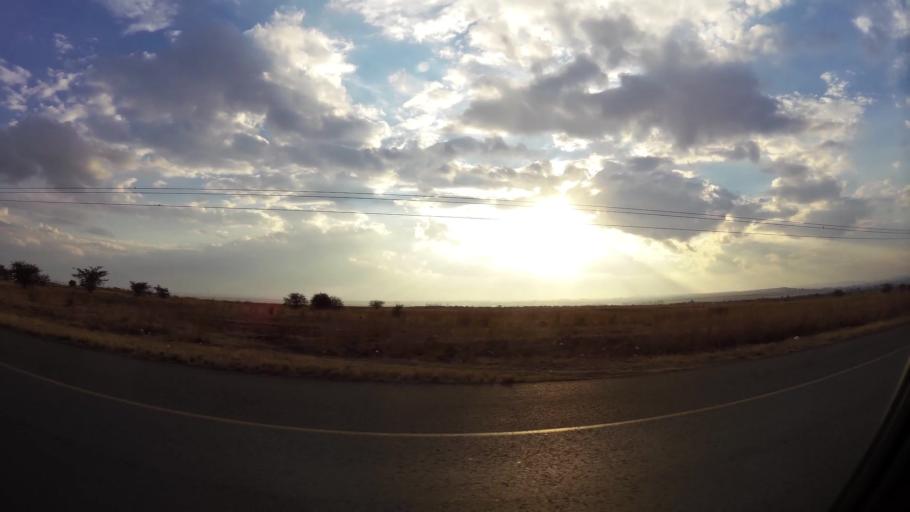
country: ZA
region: Gauteng
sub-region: Sedibeng District Municipality
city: Vanderbijlpark
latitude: -26.5942
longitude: 27.8204
